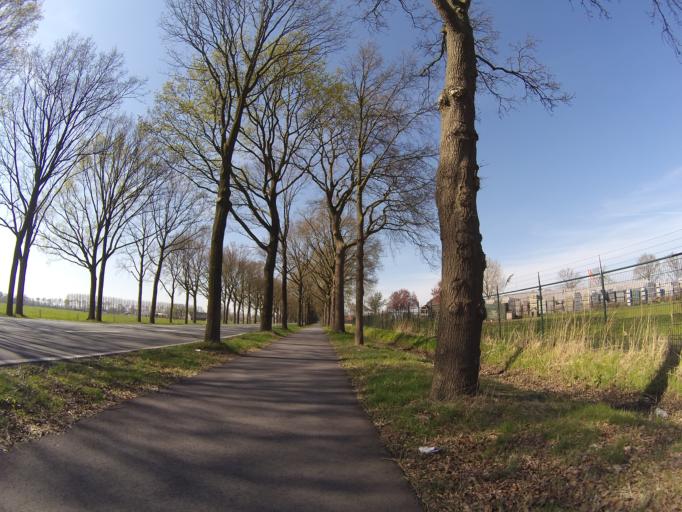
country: NL
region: Gelderland
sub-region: Gemeente Ede
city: Ederveen
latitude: 52.0517
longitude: 5.5685
